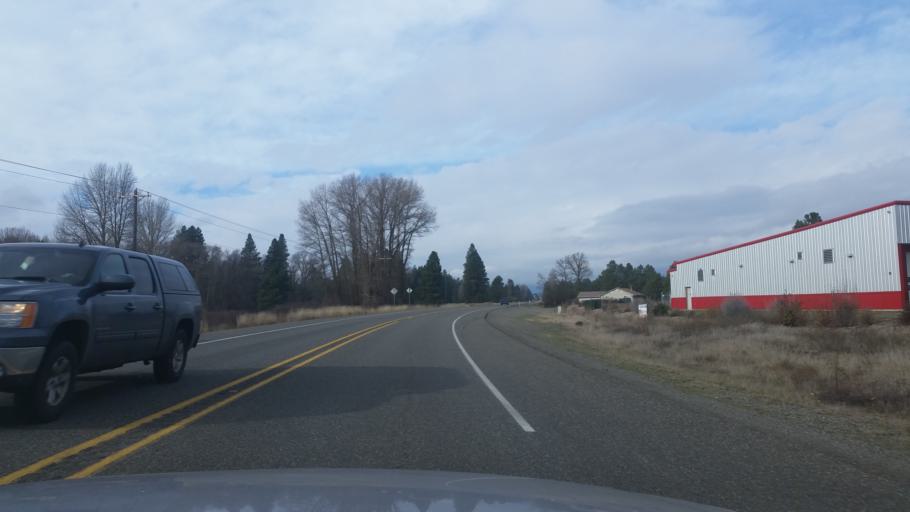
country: US
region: Washington
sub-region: Kittitas County
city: Cle Elum
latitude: 47.1752
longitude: -120.8569
